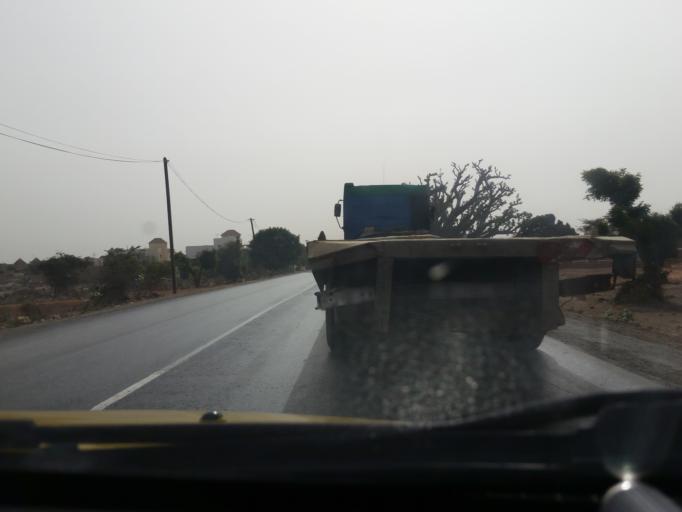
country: SN
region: Thies
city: Pout
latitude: 14.7347
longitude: -17.1523
